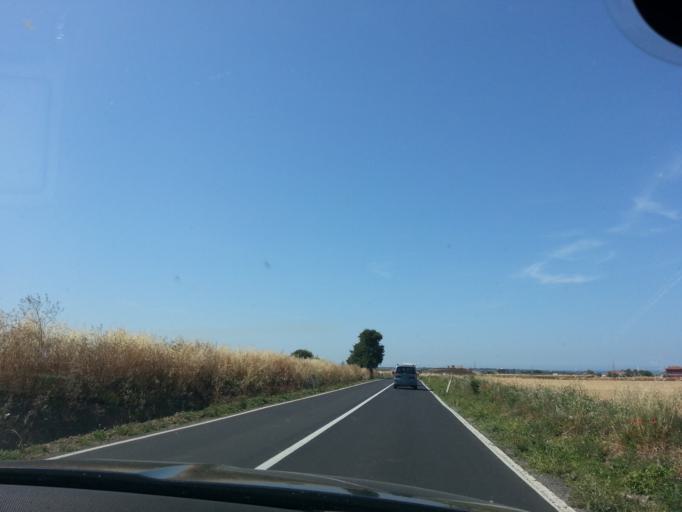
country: IT
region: Latium
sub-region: Provincia di Viterbo
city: Tarquinia
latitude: 42.2157
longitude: 11.7828
